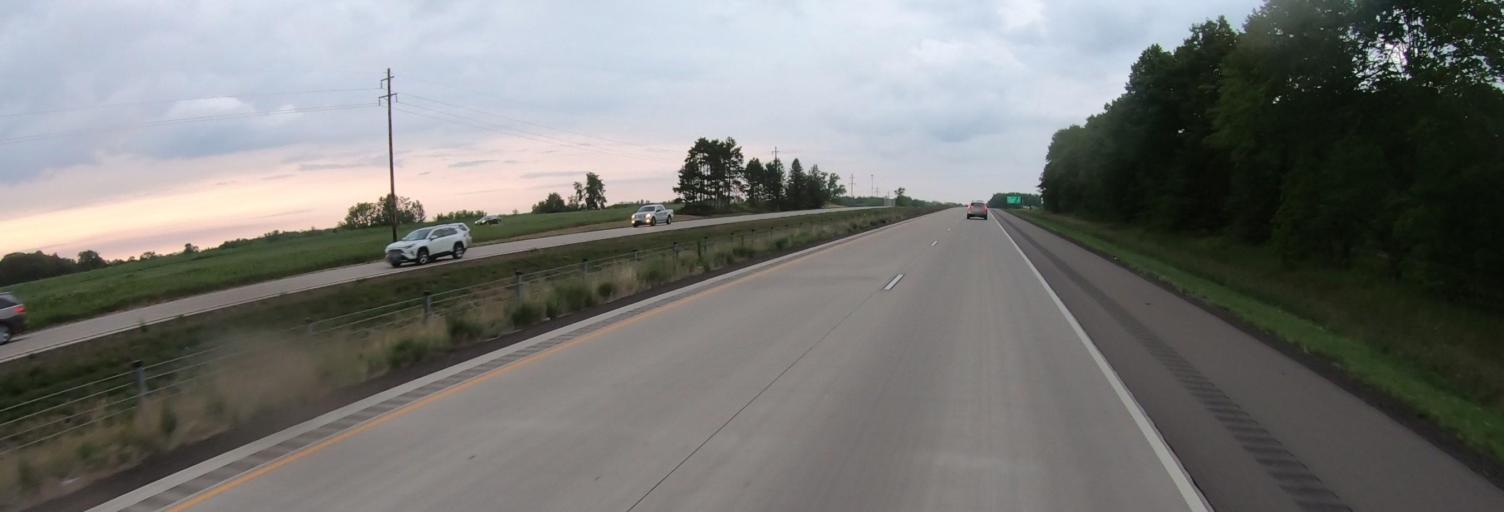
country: US
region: Minnesota
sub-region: Pine County
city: Rock Creek
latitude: 45.7795
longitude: -92.9902
